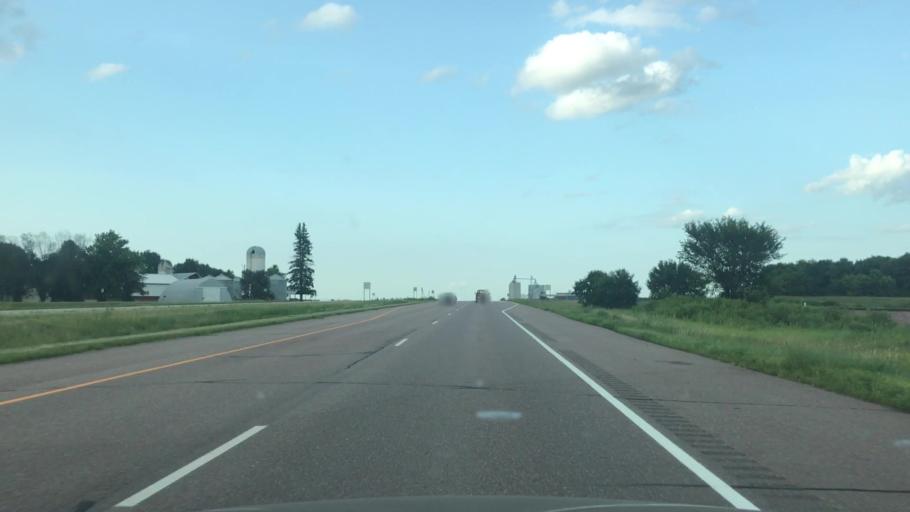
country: US
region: Minnesota
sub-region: Nobles County
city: Worthington
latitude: 43.6872
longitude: -95.4890
